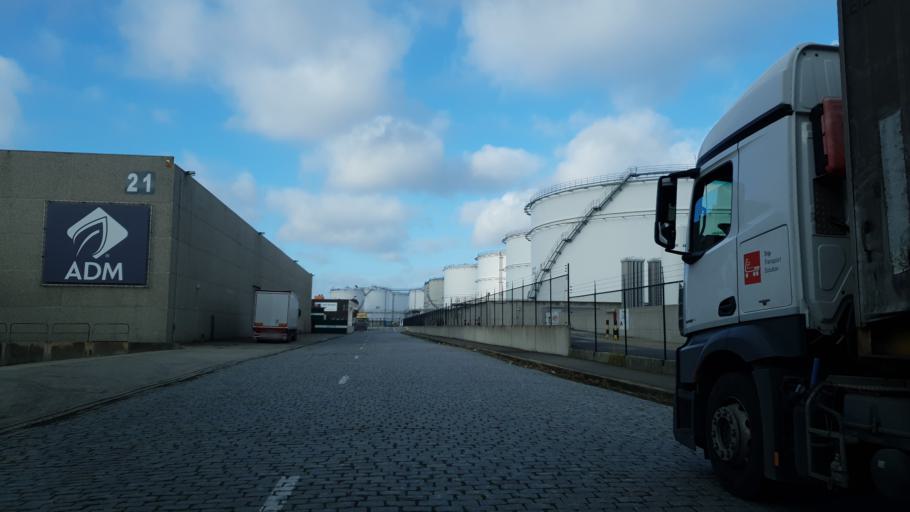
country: BE
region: Flanders
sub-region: Provincie Antwerpen
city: Zwijndrecht
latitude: 51.2707
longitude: 4.3523
